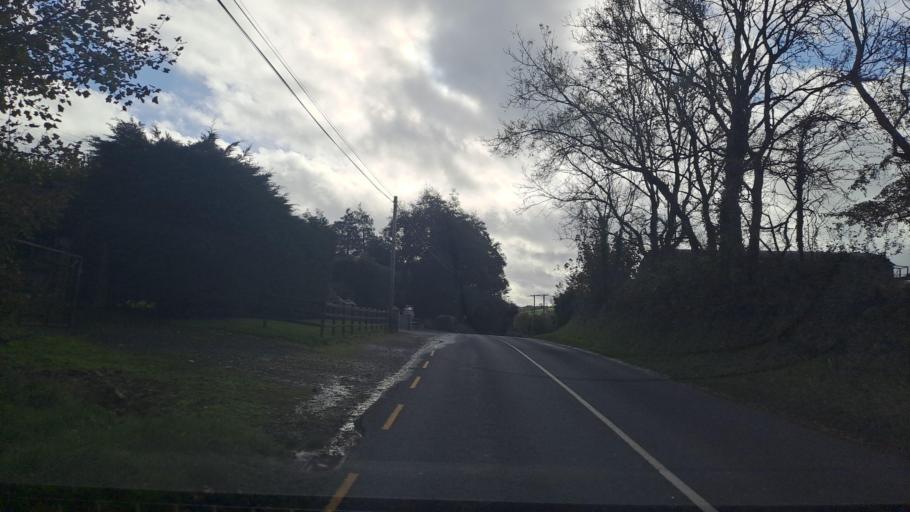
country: IE
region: Ulster
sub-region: County Monaghan
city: Monaghan
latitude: 54.2038
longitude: -6.9863
